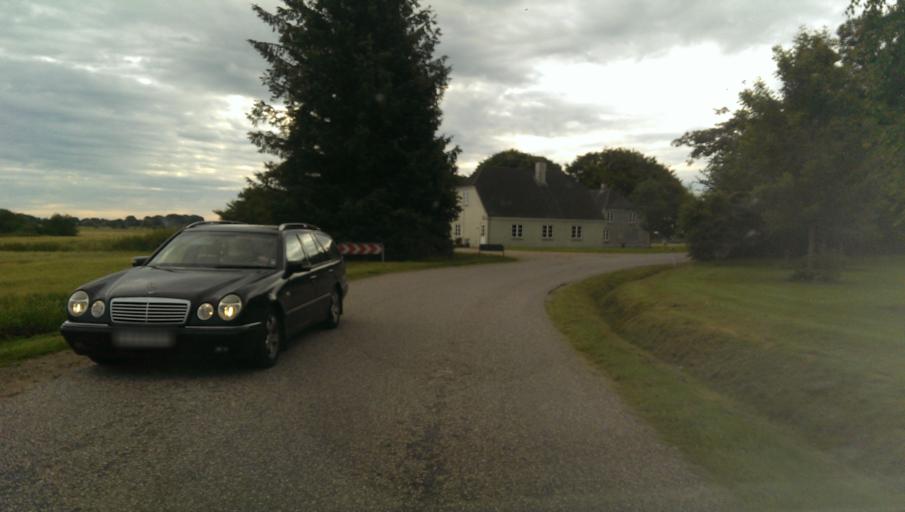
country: DK
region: South Denmark
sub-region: Esbjerg Kommune
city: Tjaereborg
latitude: 55.5125
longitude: 8.5293
